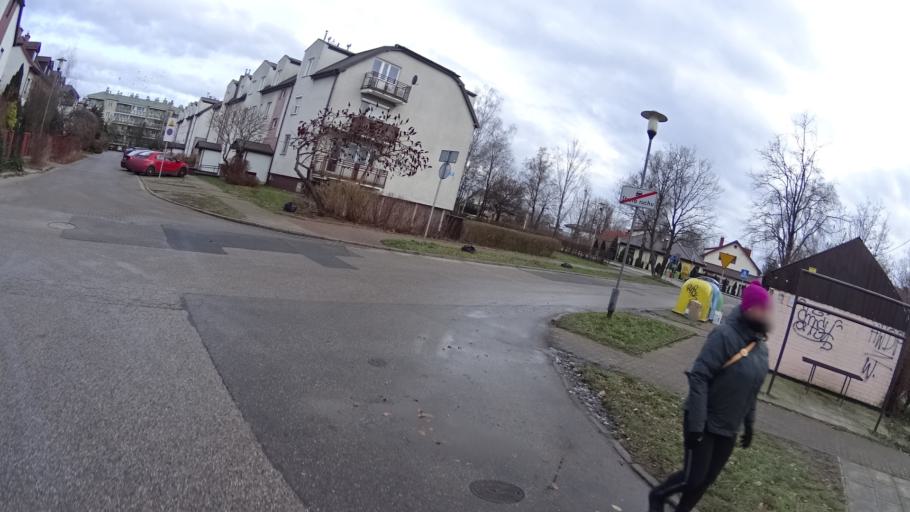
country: PL
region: Masovian Voivodeship
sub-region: Powiat pruszkowski
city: Granica
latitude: 52.1505
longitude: 20.7935
